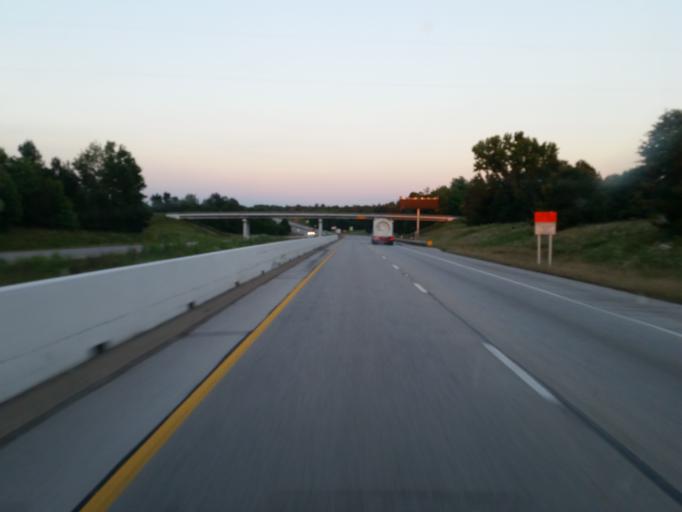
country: US
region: Texas
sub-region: Smith County
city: Hideaway
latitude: 32.4725
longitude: -95.4682
